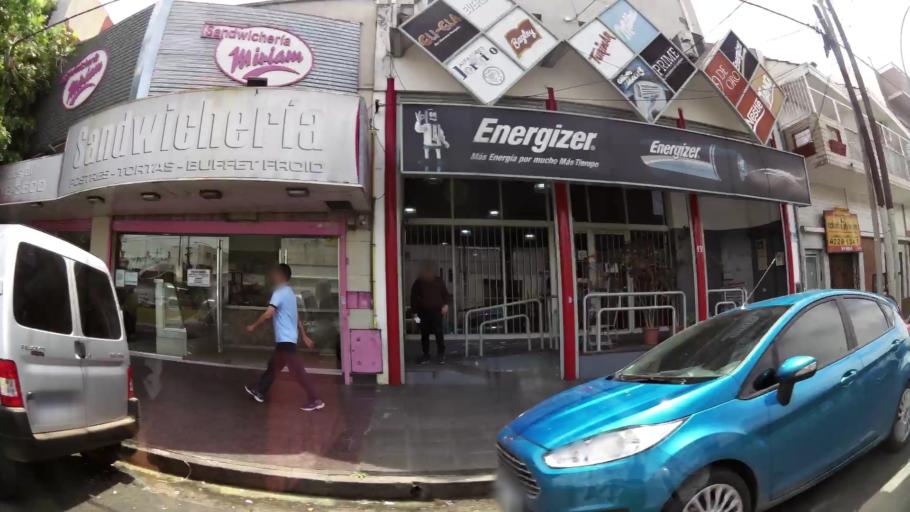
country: AR
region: Buenos Aires
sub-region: Partido de Lanus
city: Lanus
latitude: -34.6789
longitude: -58.4034
